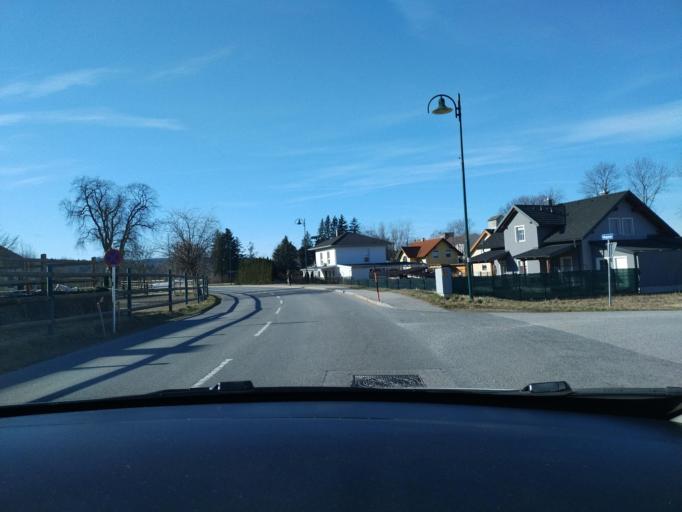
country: AT
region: Lower Austria
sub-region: Politischer Bezirk Wiener Neustadt
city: Lanzenkirchen
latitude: 47.7449
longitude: 16.2536
